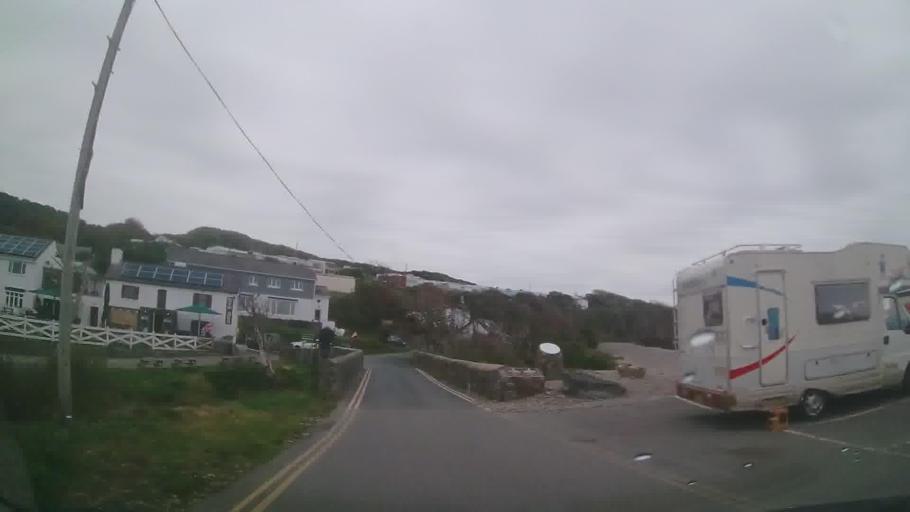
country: GB
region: Wales
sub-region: Pembrokeshire
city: Saundersfoot
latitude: 51.7340
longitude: -4.6479
